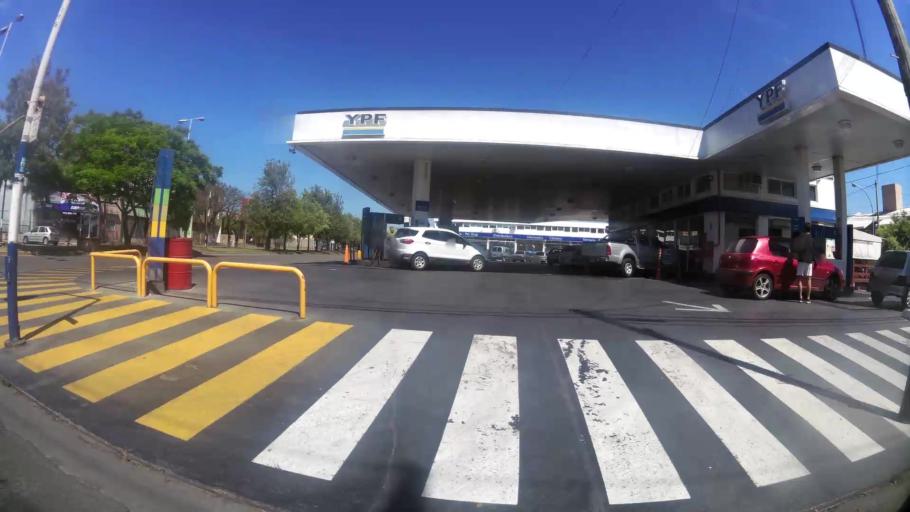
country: AR
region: Cordoba
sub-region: Departamento de Capital
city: Cordoba
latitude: -31.4194
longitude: -64.2166
